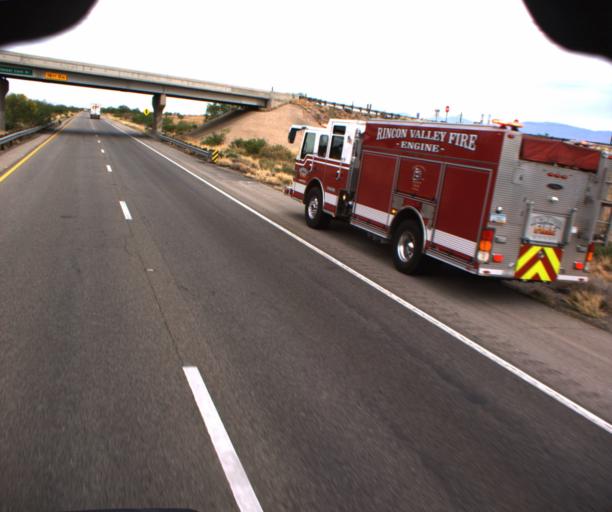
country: US
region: Arizona
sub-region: Pima County
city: Vail
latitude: 32.0280
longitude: -110.7199
